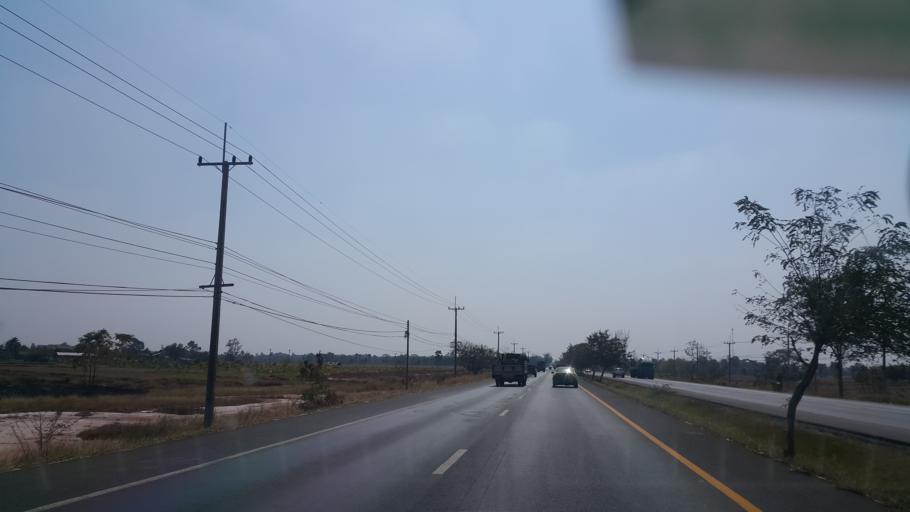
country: TH
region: Nakhon Ratchasima
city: Non Daeng
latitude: 15.4227
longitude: 102.4845
